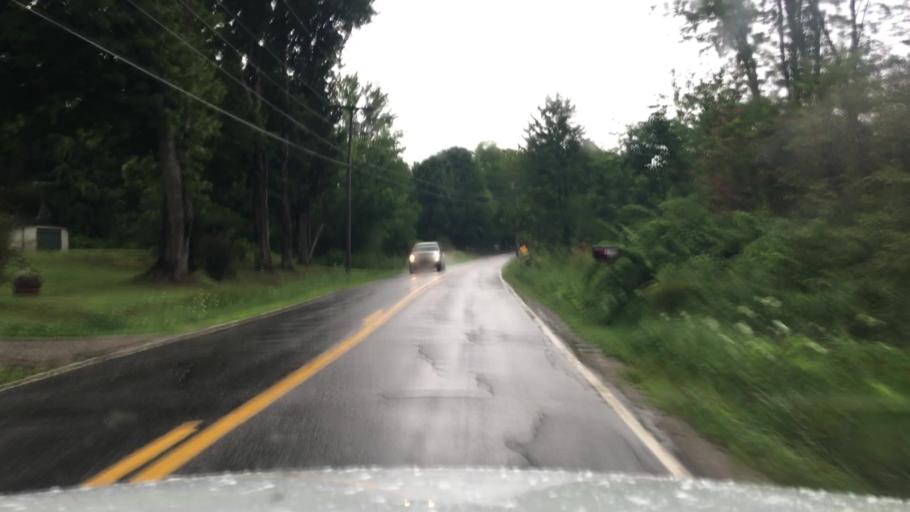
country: US
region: Maine
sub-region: Kennebec County
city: Winthrop
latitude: 44.3099
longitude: -69.9241
